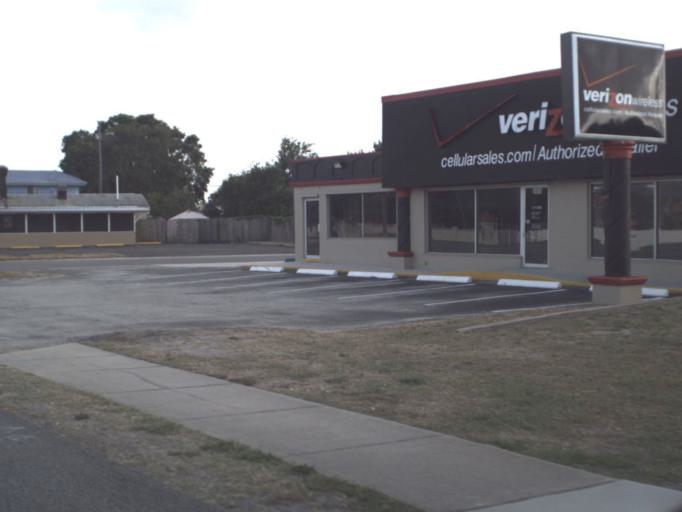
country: US
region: Florida
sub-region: Brevard County
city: Titusville
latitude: 28.5777
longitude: -80.7997
